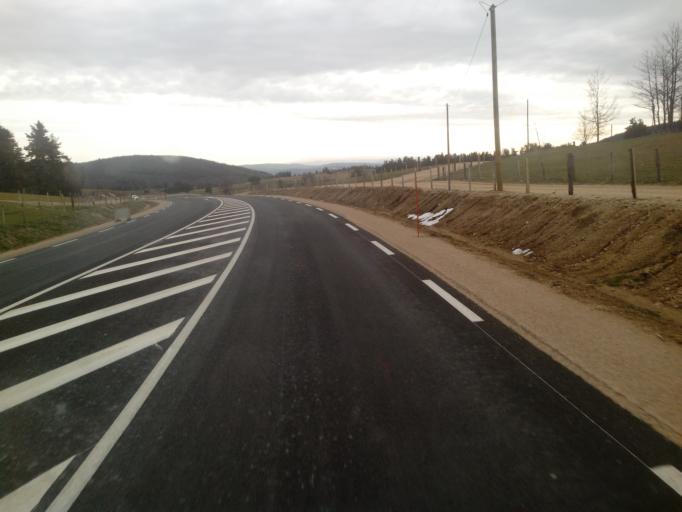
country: FR
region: Languedoc-Roussillon
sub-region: Departement de la Lozere
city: Mende
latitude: 44.5984
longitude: 3.4868
